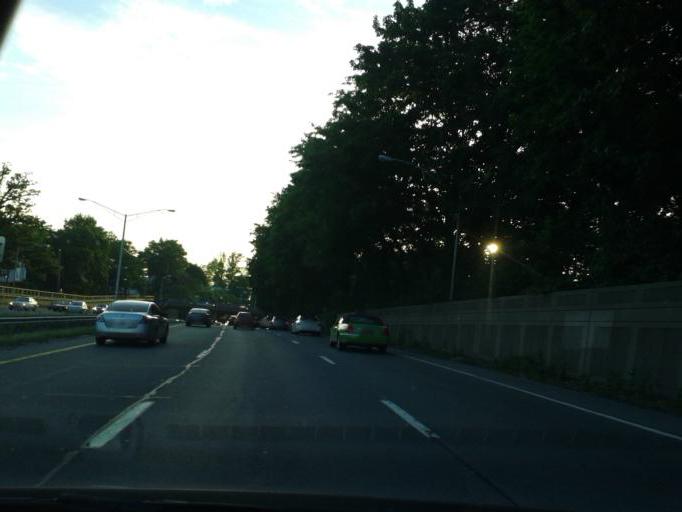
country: US
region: New York
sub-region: Westchester County
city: Bronxville
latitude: 40.9259
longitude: -73.8304
